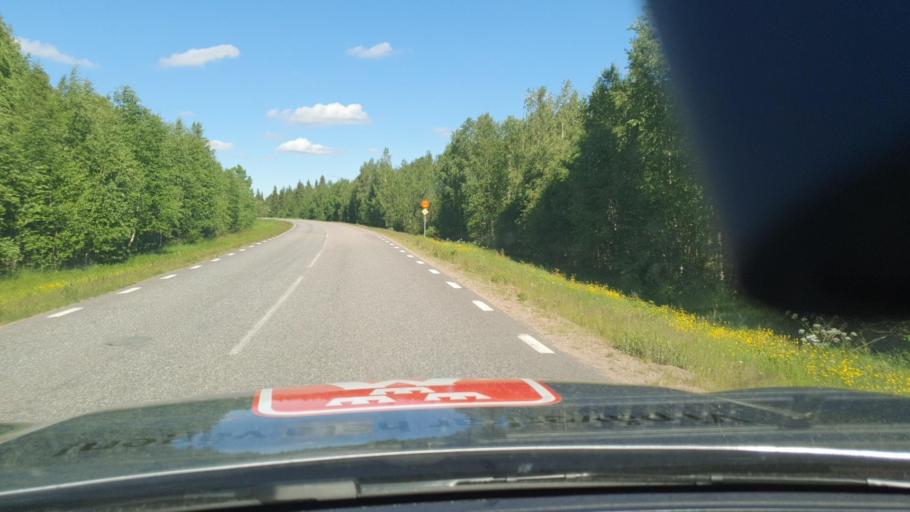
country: SE
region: Norrbotten
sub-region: Overkalix Kommun
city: OEverkalix
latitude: 66.9097
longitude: 22.7741
